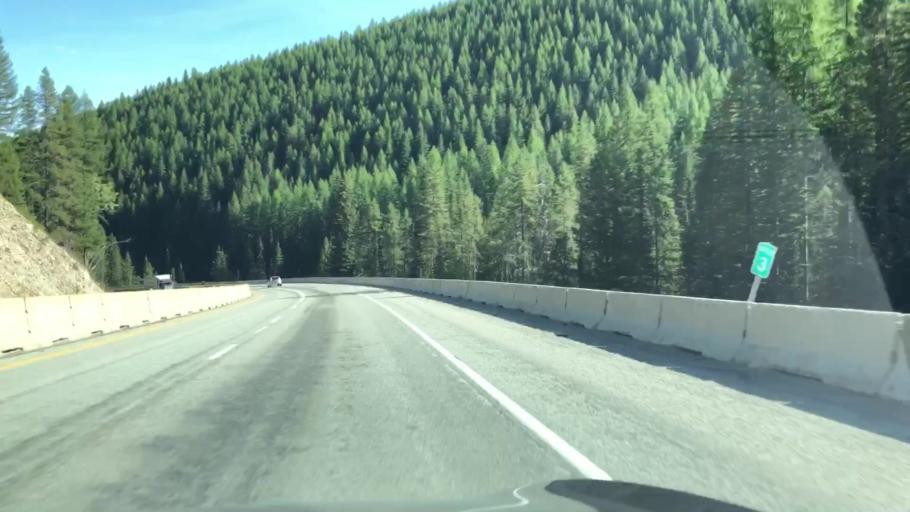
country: US
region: Idaho
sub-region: Shoshone County
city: Wallace
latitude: 47.4338
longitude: -115.6537
